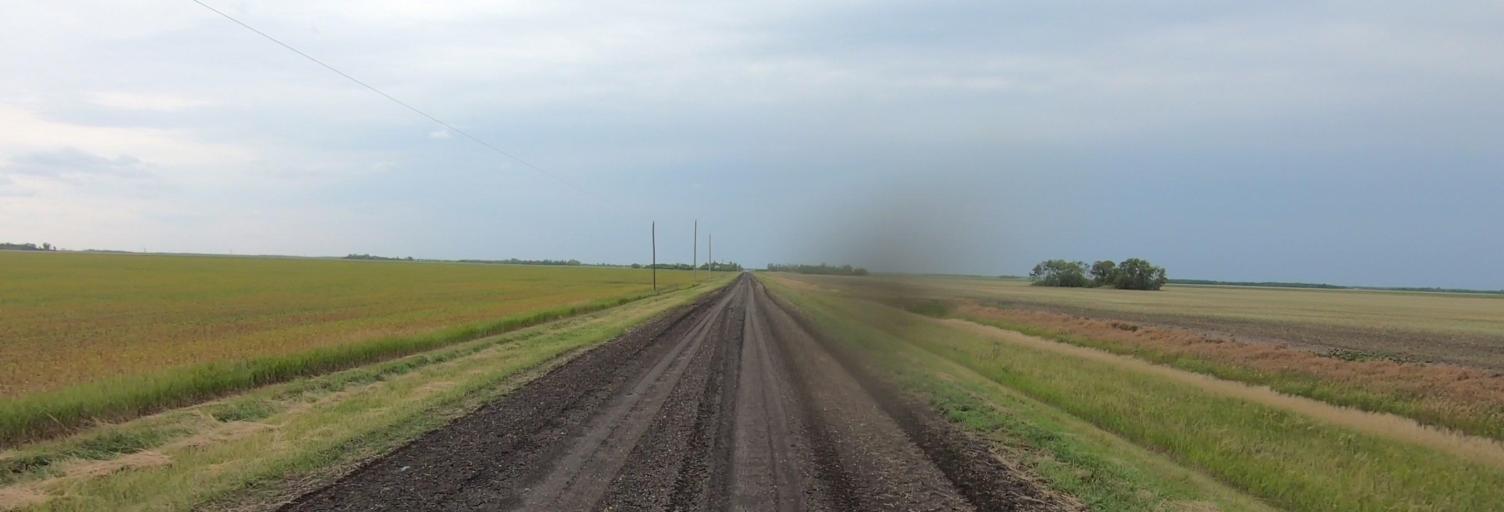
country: CA
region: Manitoba
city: Headingley
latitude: 49.7476
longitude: -97.4135
